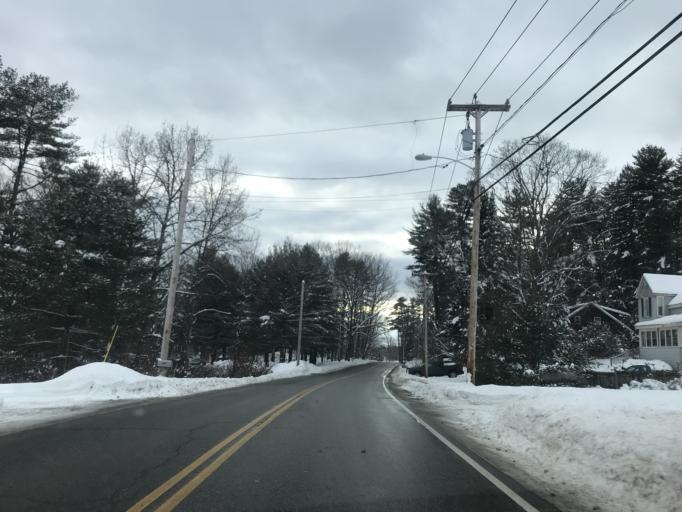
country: US
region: Maine
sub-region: Cumberland County
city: Westbrook
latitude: 43.7211
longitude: -70.3216
